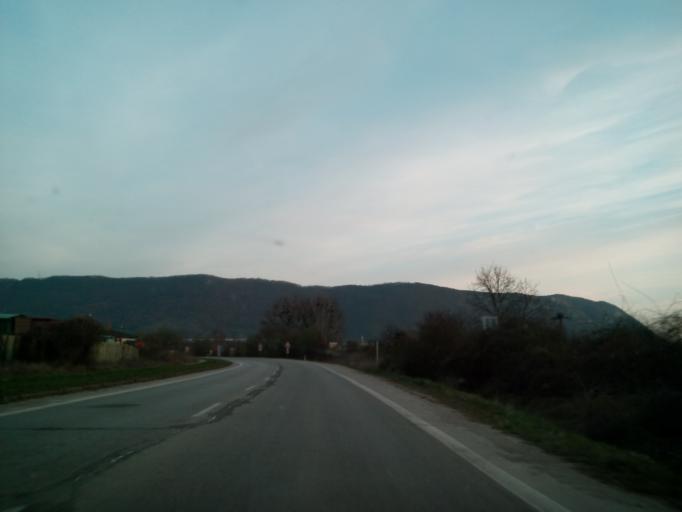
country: SK
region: Kosicky
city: Roznava
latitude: 48.6487
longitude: 20.5225
